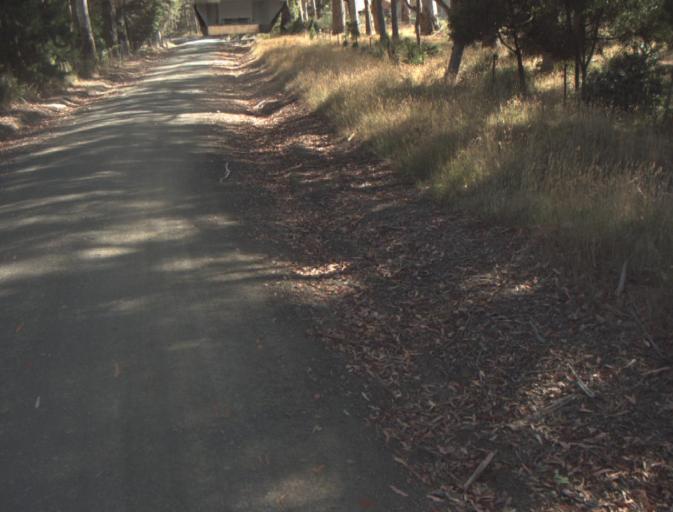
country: AU
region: Tasmania
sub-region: Launceston
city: Newstead
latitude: -41.3272
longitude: 147.3418
